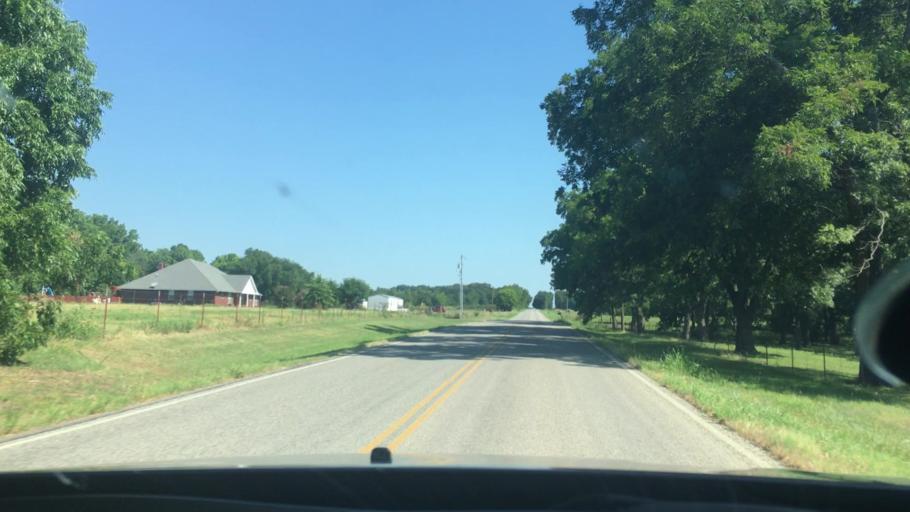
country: US
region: Oklahoma
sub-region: Johnston County
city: Tishomingo
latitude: 34.2891
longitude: -96.6185
